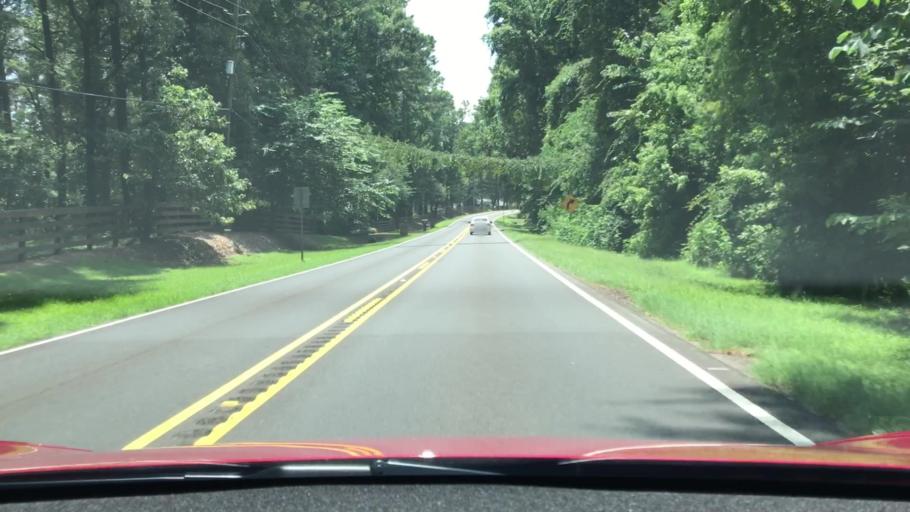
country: US
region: Louisiana
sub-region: Bossier Parish
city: Bossier City
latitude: 32.3666
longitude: -93.6868
